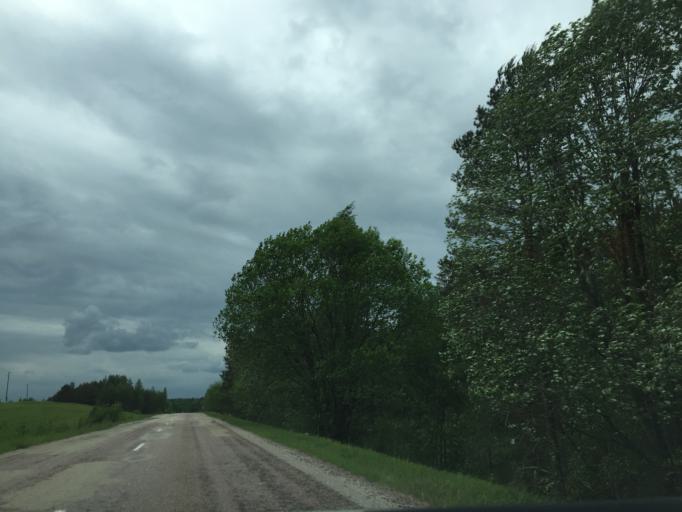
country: LV
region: Aglona
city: Aglona
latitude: 56.1482
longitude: 27.1780
